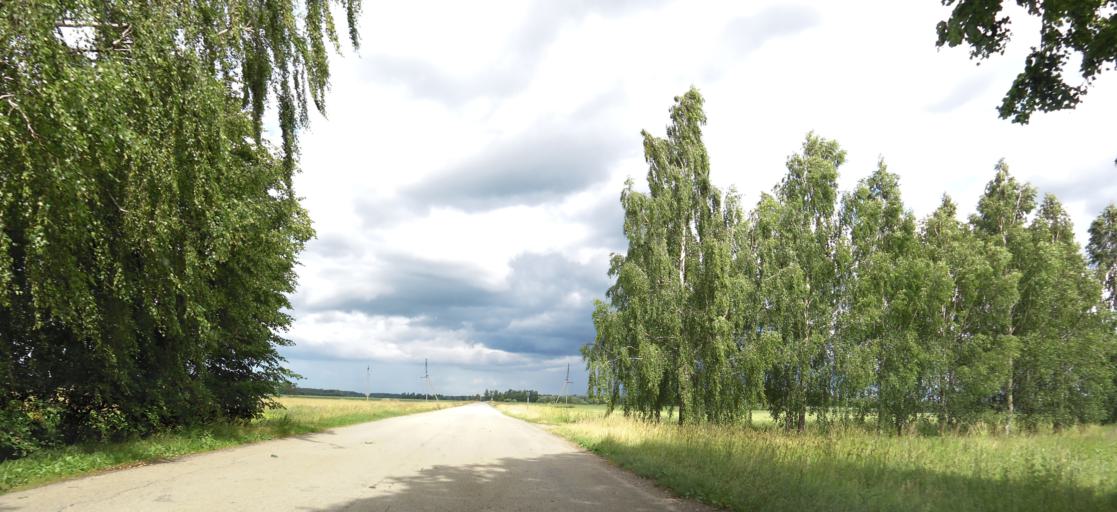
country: LT
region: Panevezys
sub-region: Birzai
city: Birzai
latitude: 56.3193
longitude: 24.8090
